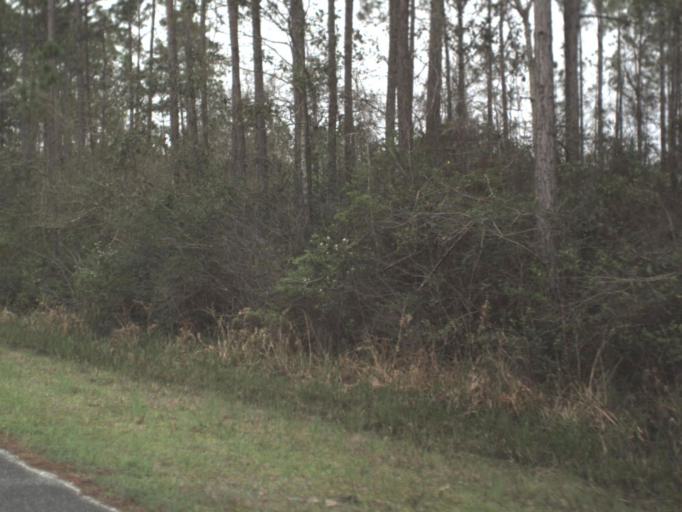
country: US
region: Florida
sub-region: Franklin County
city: Eastpoint
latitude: 29.8287
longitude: -84.8675
